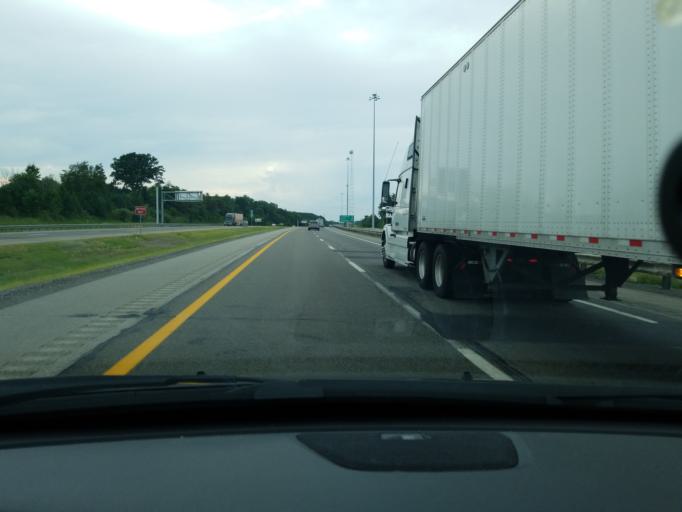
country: US
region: Ohio
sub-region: Mahoning County
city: New Middletown
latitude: 40.9258
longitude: -80.5597
